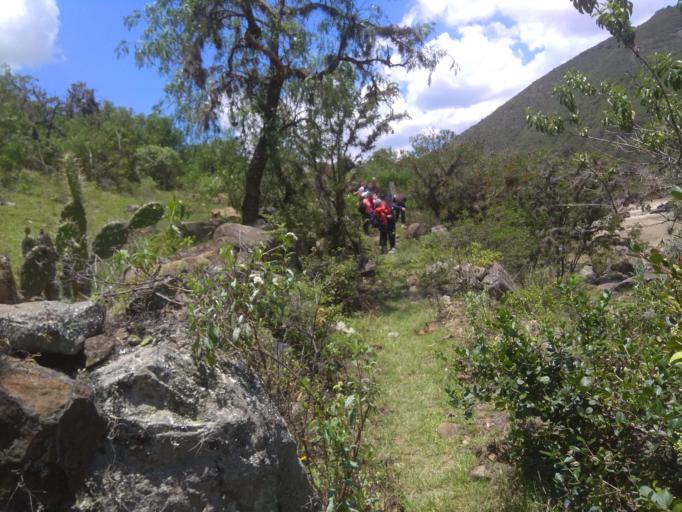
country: CO
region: Boyaca
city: Socha Viejo
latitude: 5.9968
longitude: -72.7174
